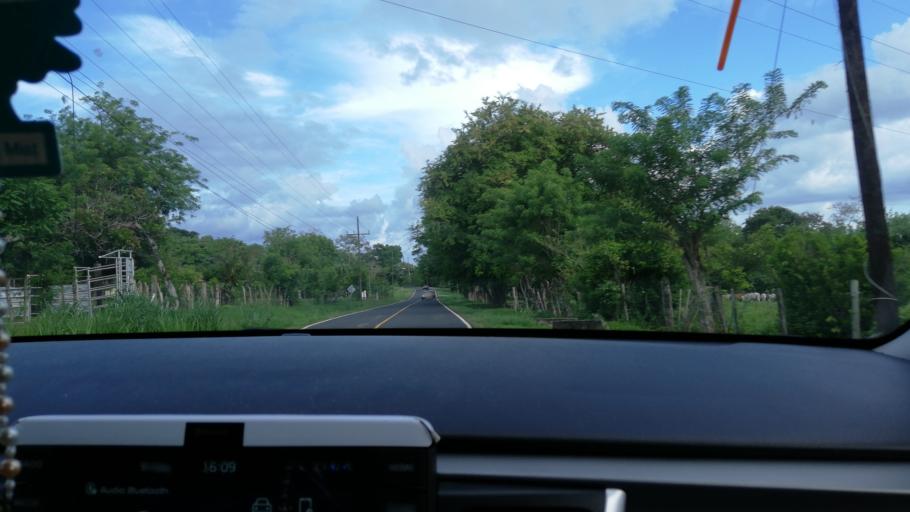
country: PA
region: Panama
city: Las Colinas
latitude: 8.4901
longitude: -80.0230
